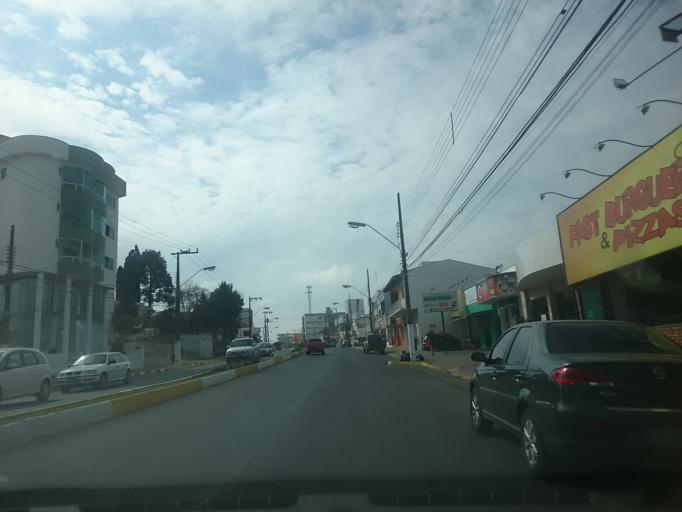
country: BR
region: Santa Catarina
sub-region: Lages
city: Lages
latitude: -27.8119
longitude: -50.3097
